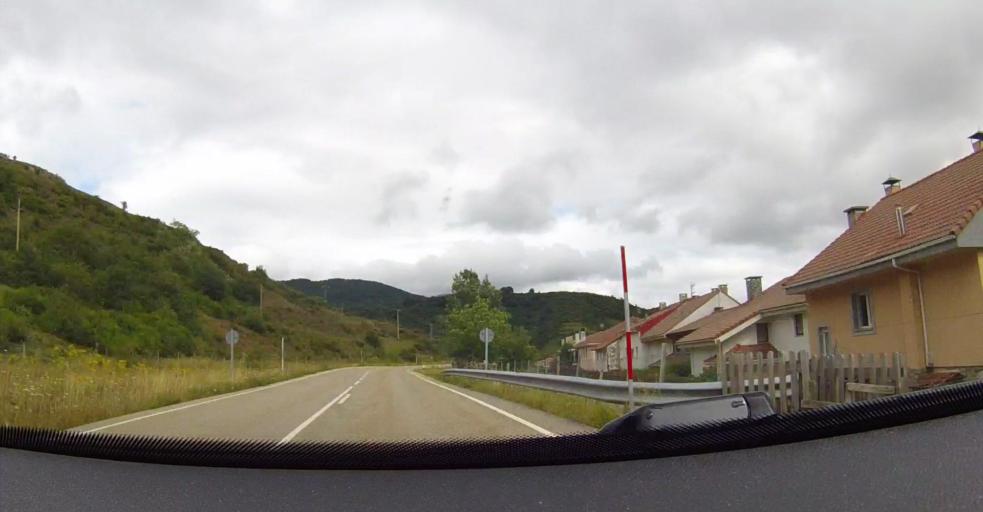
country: ES
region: Castille and Leon
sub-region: Provincia de Leon
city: Buron
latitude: 43.0253
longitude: -5.0530
